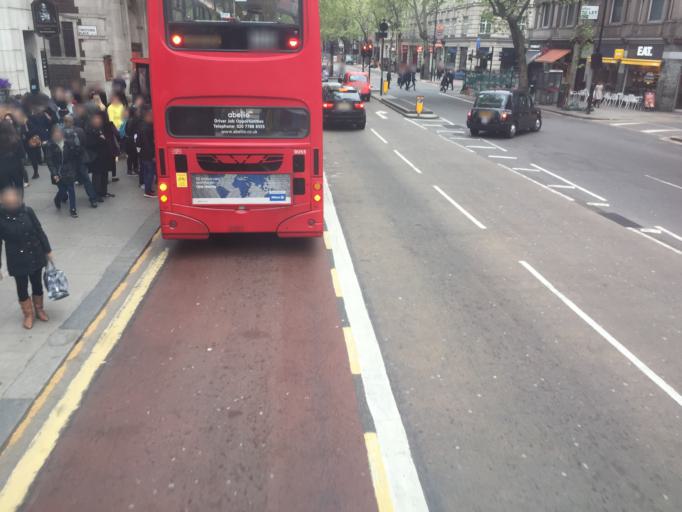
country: GB
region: England
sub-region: Greater London
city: London
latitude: 51.5169
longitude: -0.1200
